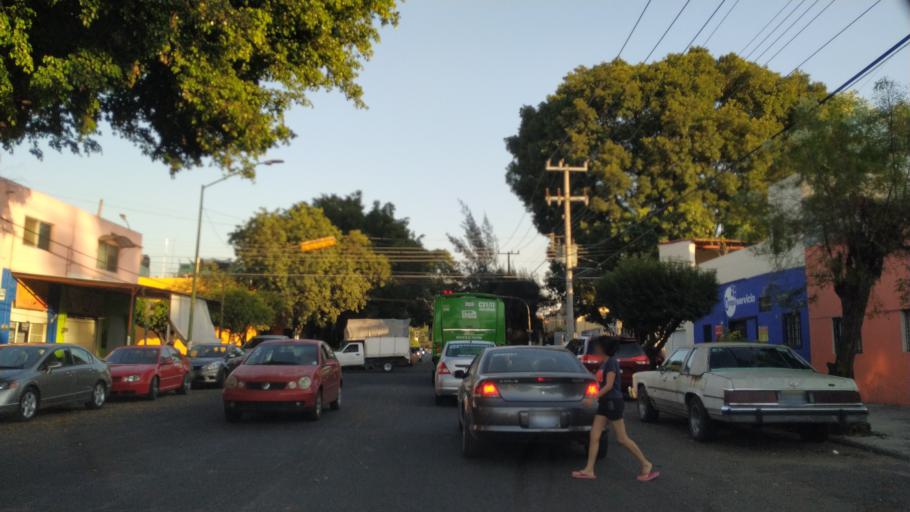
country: MX
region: Jalisco
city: Tlaquepaque
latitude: 20.6556
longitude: -103.3299
